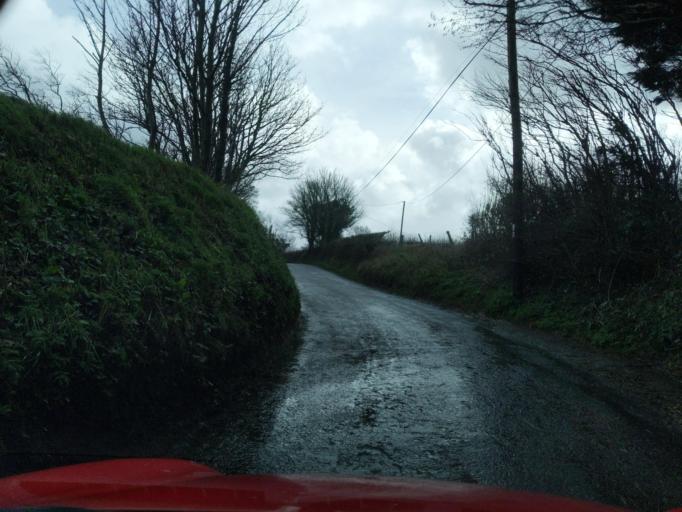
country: GB
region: England
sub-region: Devon
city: Ivybridge
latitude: 50.3736
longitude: -3.9387
